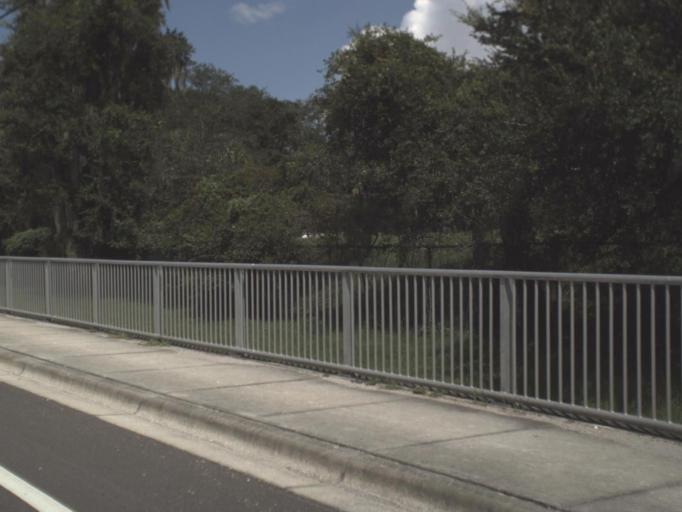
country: US
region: Florida
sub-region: Hillsborough County
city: Palm River-Clair Mel
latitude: 27.9228
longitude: -82.3836
